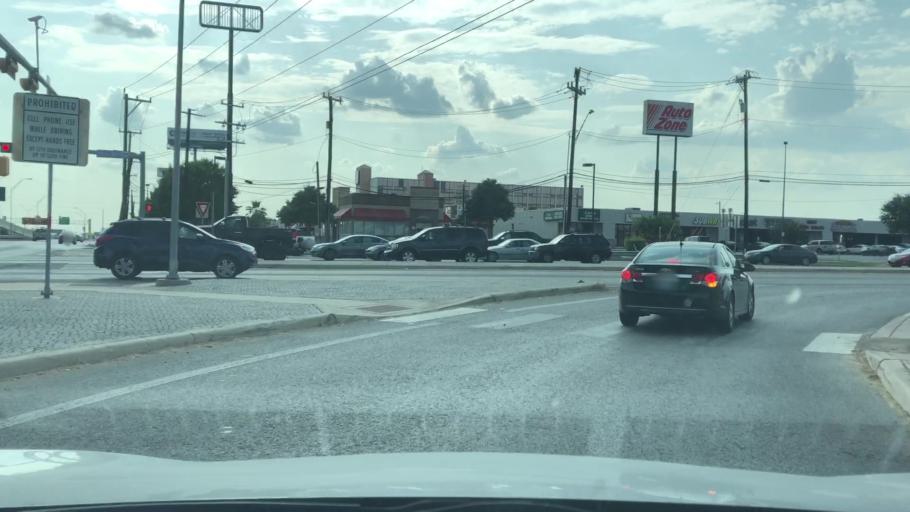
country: US
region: Texas
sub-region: Bexar County
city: Windcrest
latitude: 29.5164
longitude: -98.4107
